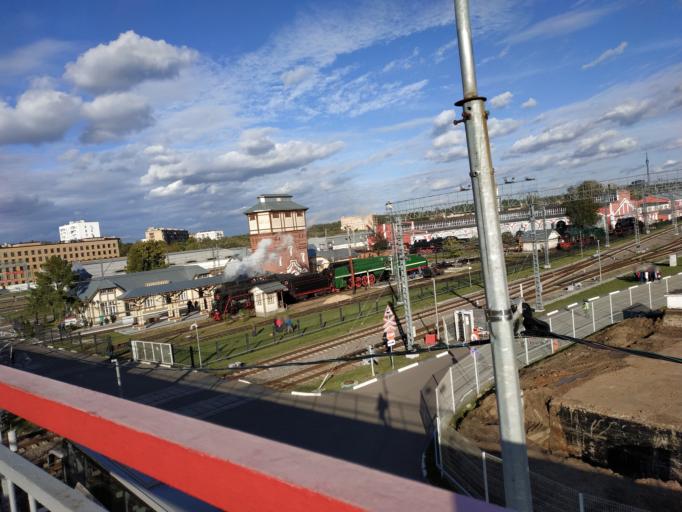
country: RU
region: Moskovskaya
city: Koptevo
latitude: 55.8134
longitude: 37.5272
